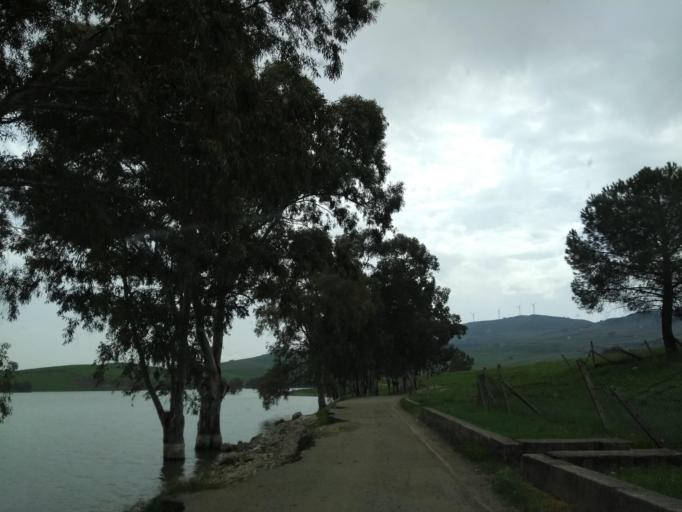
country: IT
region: Sicily
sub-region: Palermo
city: Partinico
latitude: 37.9915
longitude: 13.0825
